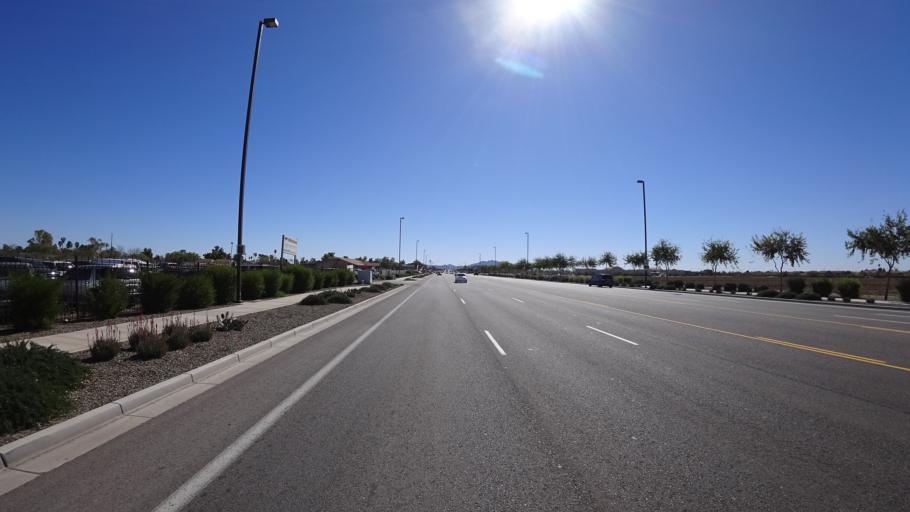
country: US
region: Arizona
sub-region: Maricopa County
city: Queen Creek
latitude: 33.3174
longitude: -111.6867
